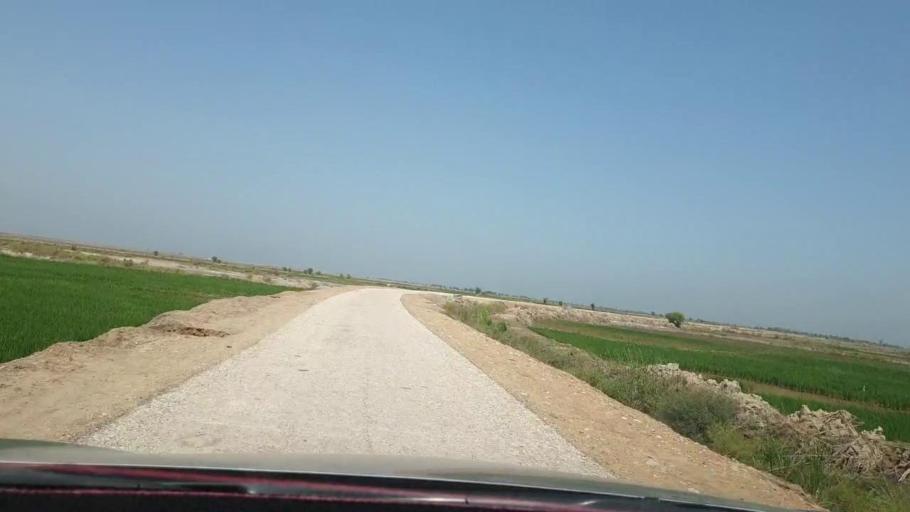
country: PK
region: Sindh
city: Warah
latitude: 27.5284
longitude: 67.7124
